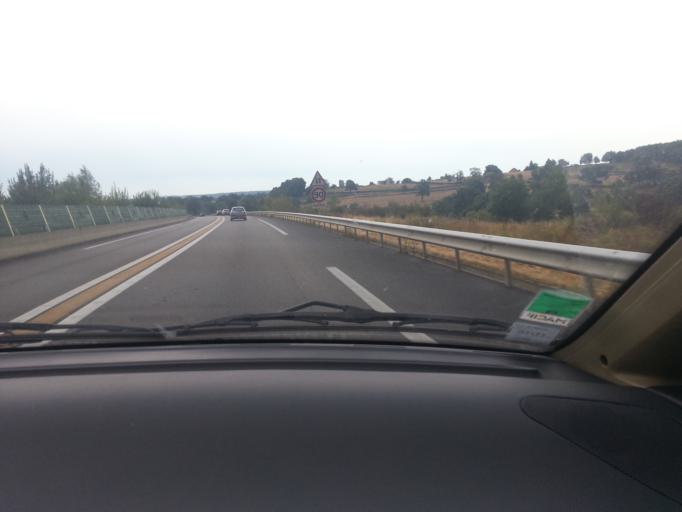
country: FR
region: Auvergne
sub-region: Departement de l'Allier
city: Molinet
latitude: 46.4560
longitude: 3.9244
